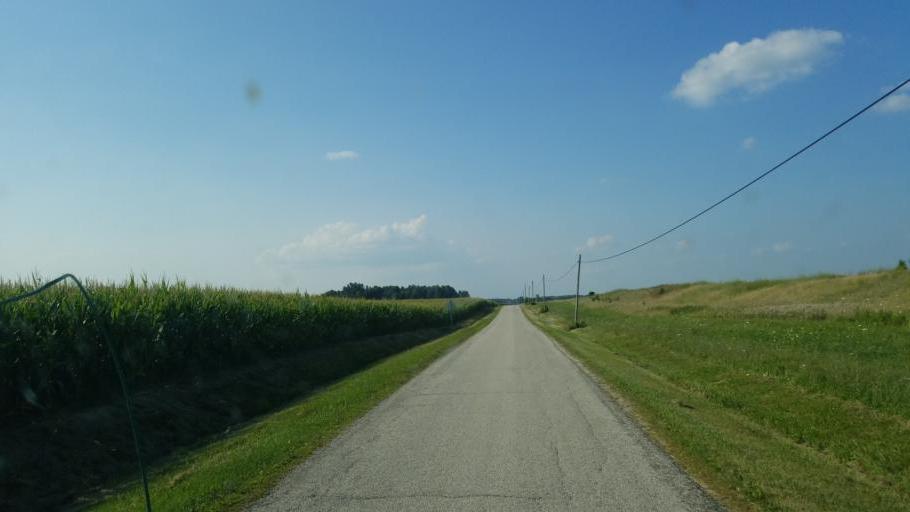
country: US
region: Ohio
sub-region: Crawford County
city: Bucyrus
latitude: 40.8643
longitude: -83.0740
